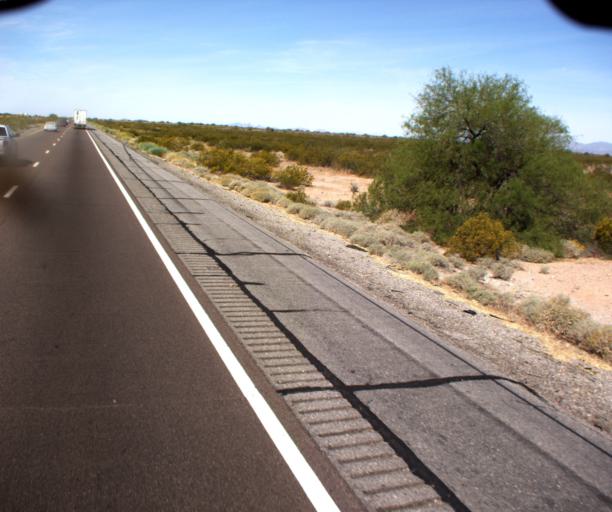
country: US
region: Arizona
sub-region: La Paz County
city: Salome
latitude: 33.5496
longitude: -113.2235
